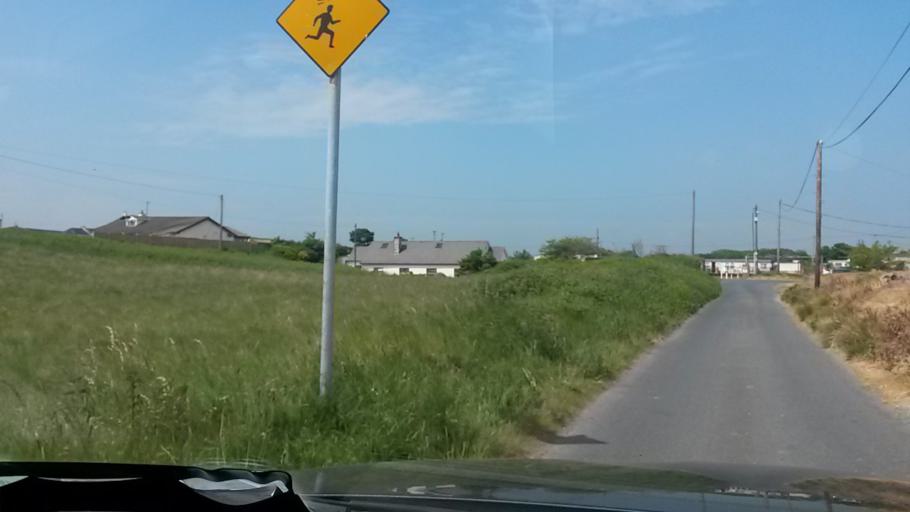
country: IE
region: Leinster
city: Portraine
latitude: 53.4996
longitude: -6.1165
